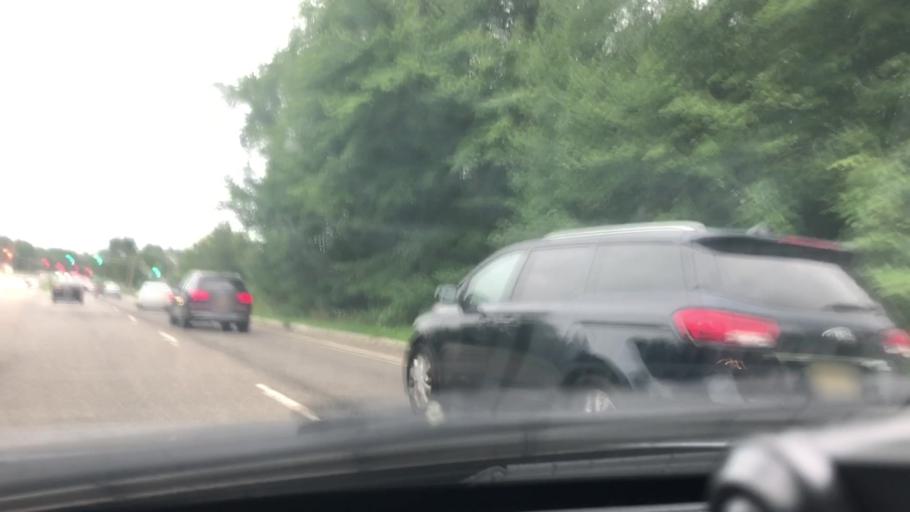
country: US
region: New Jersey
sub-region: Morris County
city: Hanover
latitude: 40.8005
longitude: -74.3413
